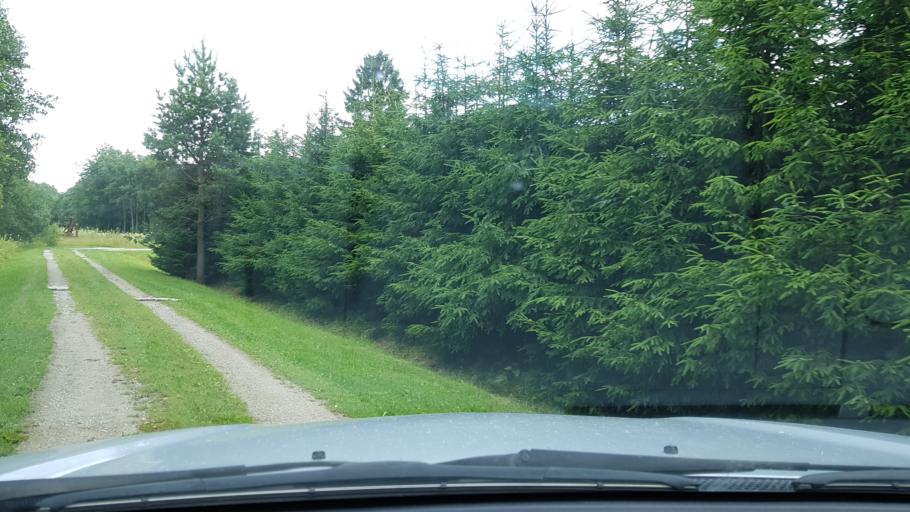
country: EE
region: Ida-Virumaa
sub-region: Narva-Joesuu linn
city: Narva-Joesuu
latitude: 59.4029
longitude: 27.9610
